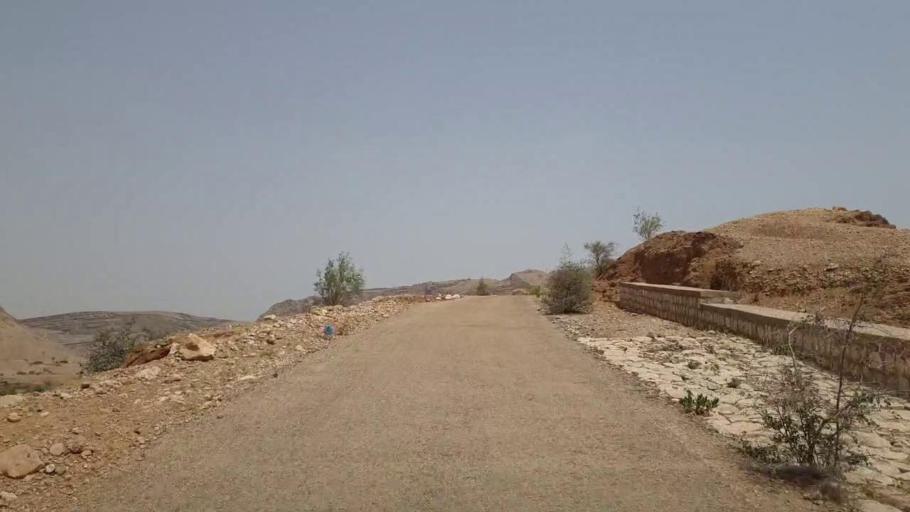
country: PK
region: Sindh
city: Sann
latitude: 25.8939
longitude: 67.9034
